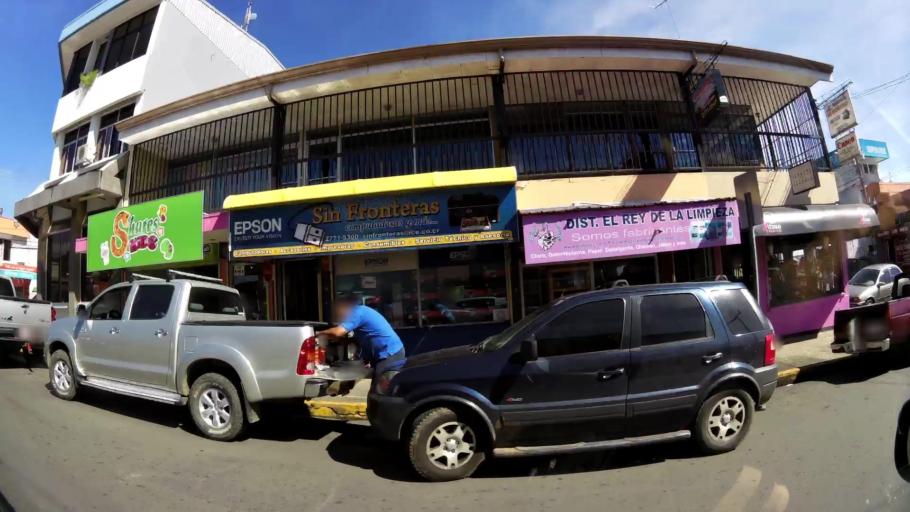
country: CR
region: San Jose
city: San Isidro
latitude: 9.3734
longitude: -83.7053
